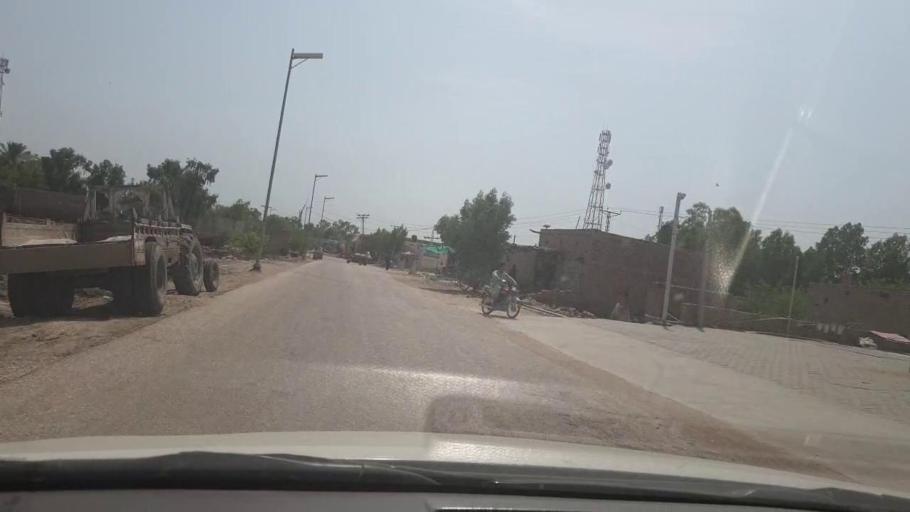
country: PK
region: Sindh
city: Garhi Yasin
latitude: 27.9113
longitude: 68.5160
